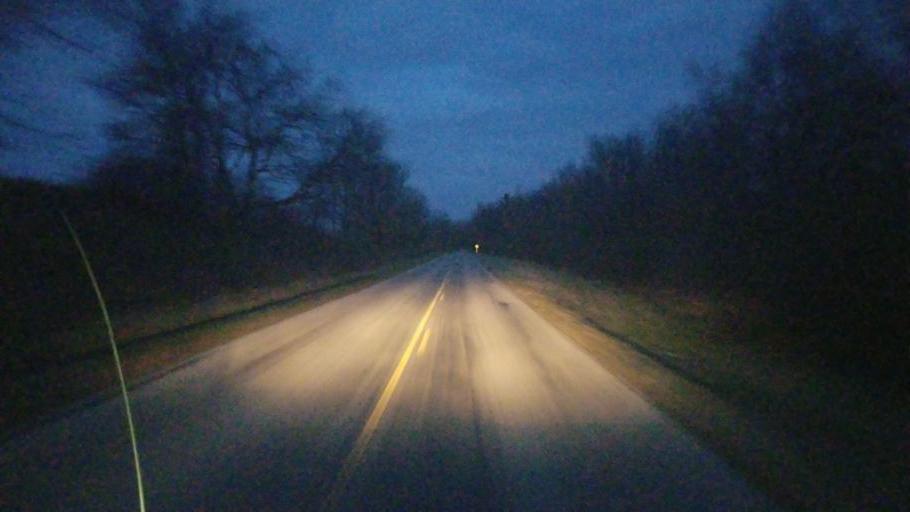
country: US
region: Ohio
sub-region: Marion County
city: Prospect
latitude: 40.4622
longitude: -83.1924
